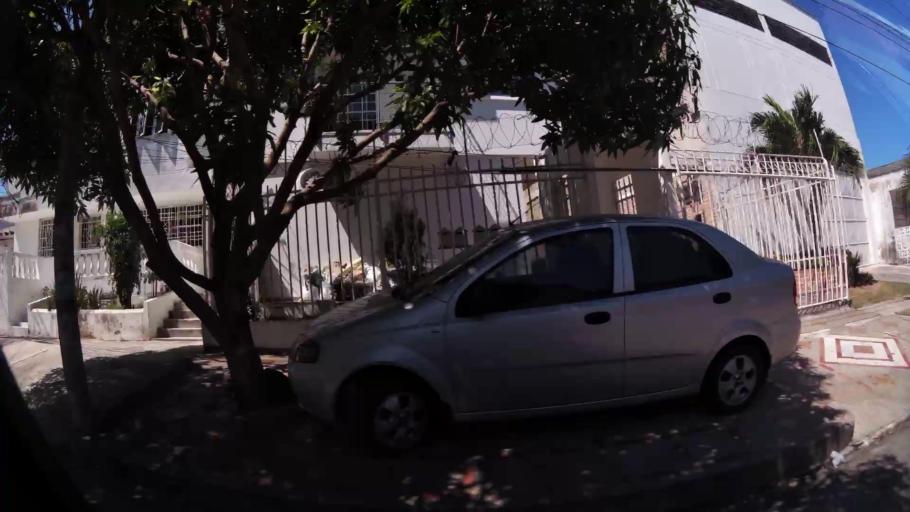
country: CO
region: Atlantico
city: Barranquilla
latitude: 10.9882
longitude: -74.8082
